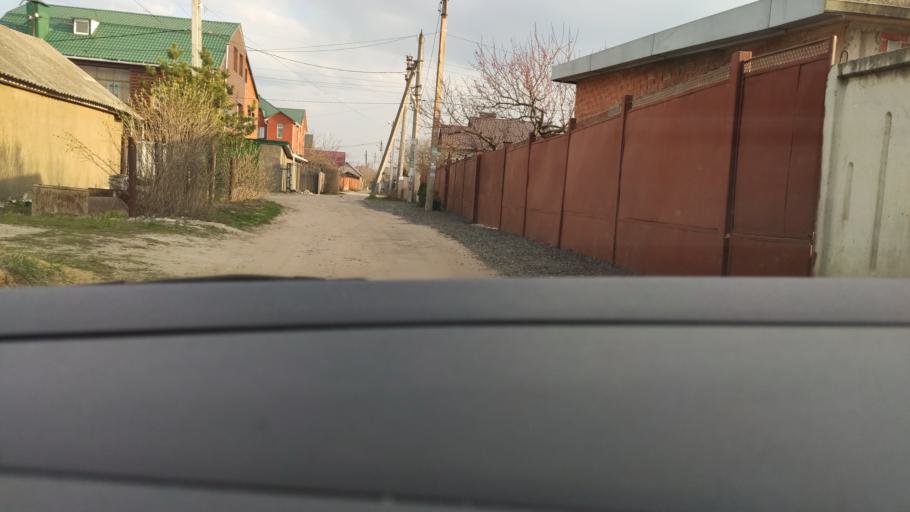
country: RU
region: Voronezj
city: Pridonskoy
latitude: 51.6594
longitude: 39.0899
